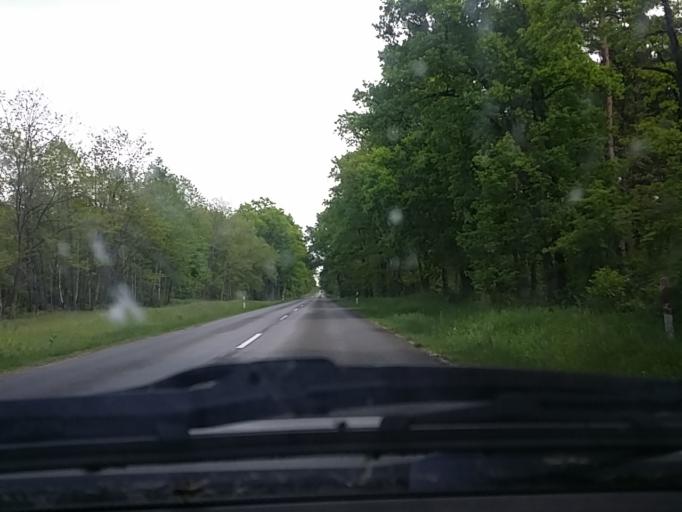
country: HU
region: Somogy
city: Barcs
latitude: 45.9758
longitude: 17.5551
